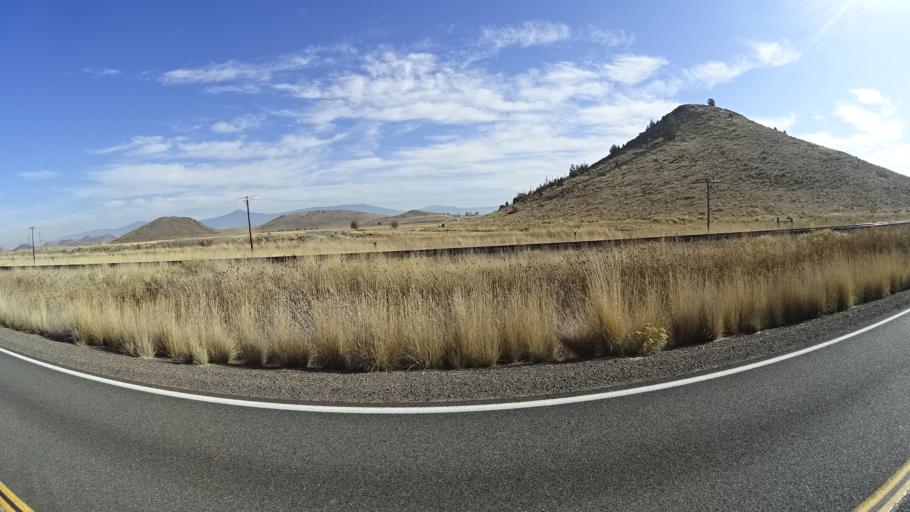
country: US
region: California
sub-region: Siskiyou County
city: Weed
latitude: 41.5359
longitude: -122.5248
